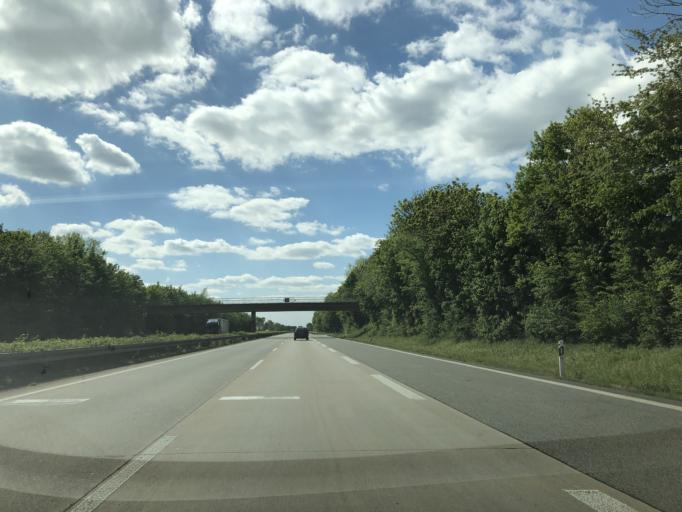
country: DE
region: North Rhine-Westphalia
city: Erwitte
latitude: 51.5871
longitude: 8.3771
